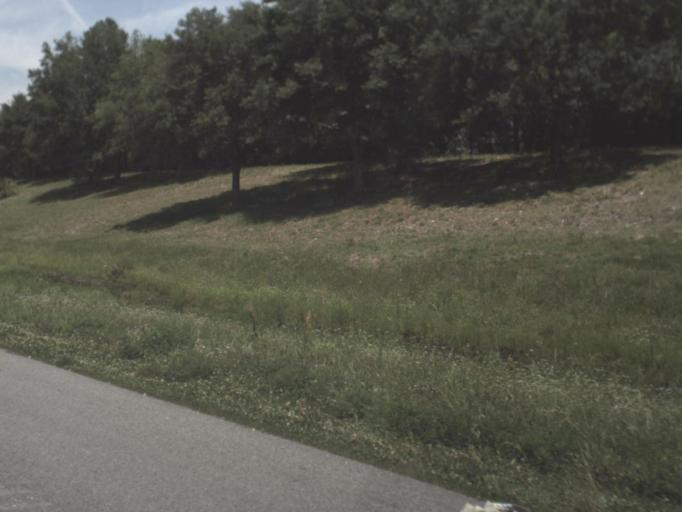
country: US
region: Florida
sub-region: Duval County
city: Jacksonville
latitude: 30.3361
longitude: -81.5366
